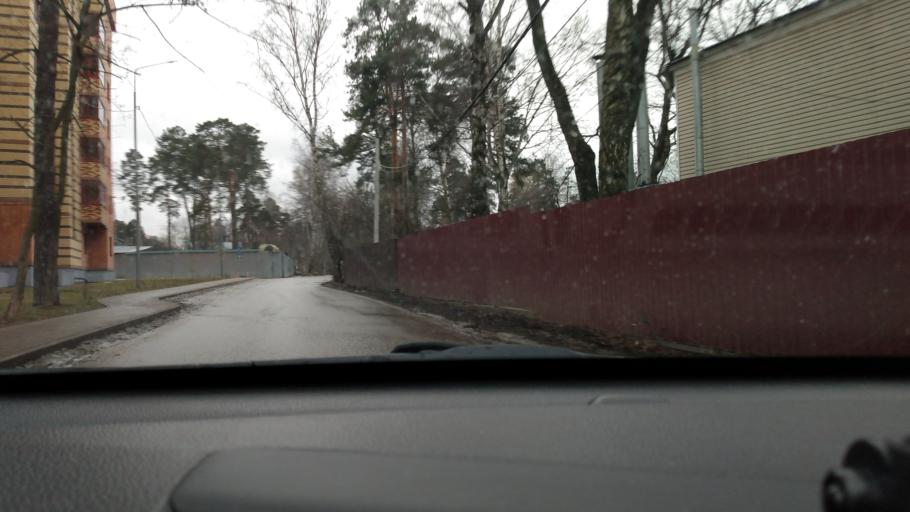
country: RU
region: Moskovskaya
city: Druzhba
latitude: 55.8964
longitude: 37.7435
